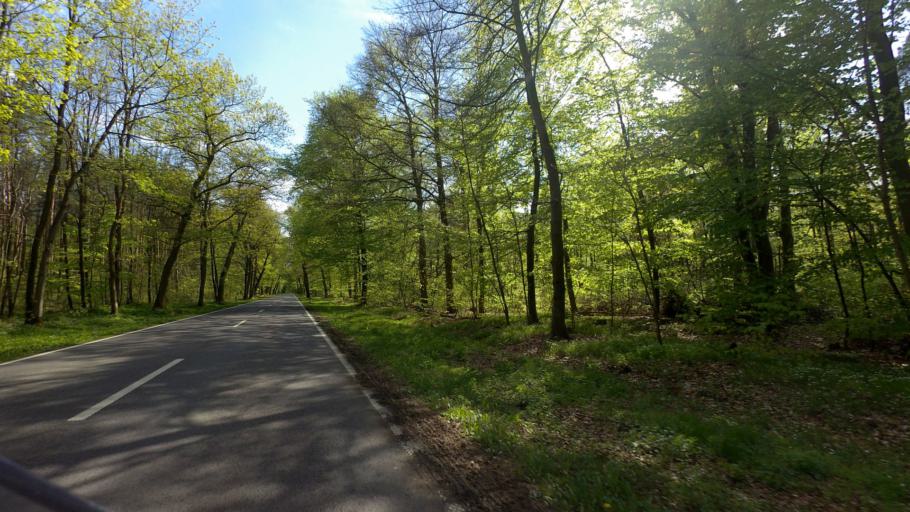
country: DE
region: Brandenburg
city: Templin
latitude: 53.0848
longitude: 13.5065
